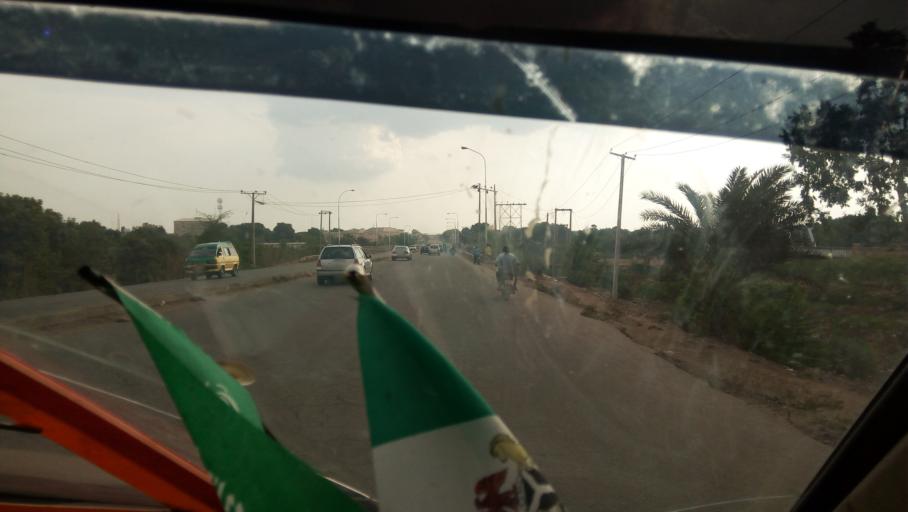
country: NG
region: Kaduna
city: Kaduna
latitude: 10.4999
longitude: 7.4233
